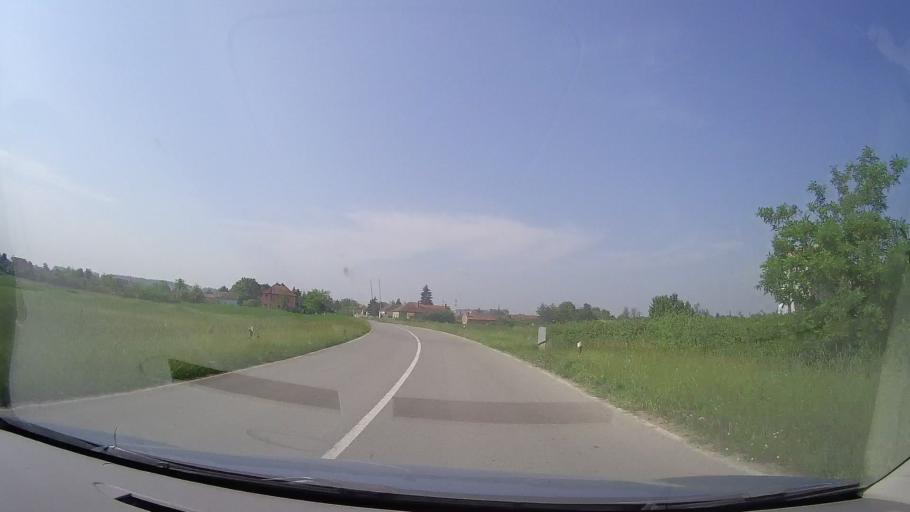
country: RS
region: Autonomna Pokrajina Vojvodina
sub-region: Srednjebanatski Okrug
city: Secanj
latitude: 45.3750
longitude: 20.7786
